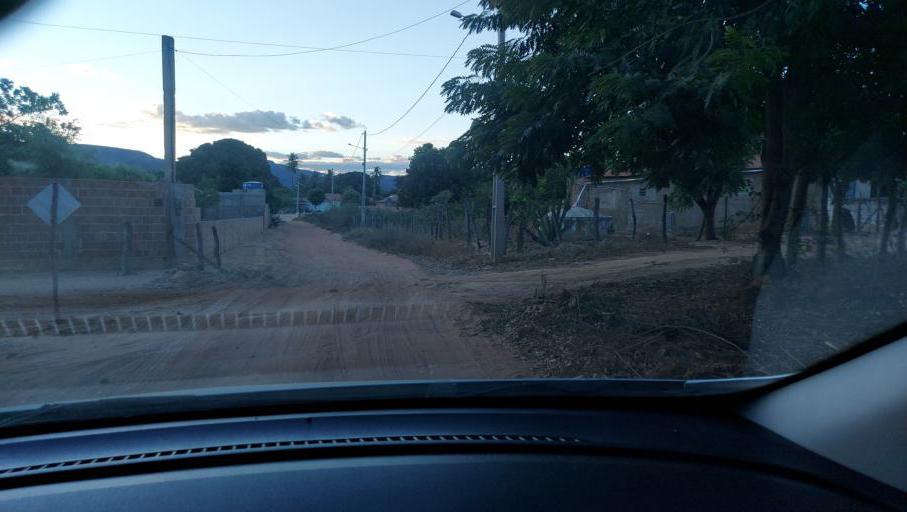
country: BR
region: Bahia
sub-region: Oliveira Dos Brejinhos
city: Beira Rio
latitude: -12.0904
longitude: -42.5627
